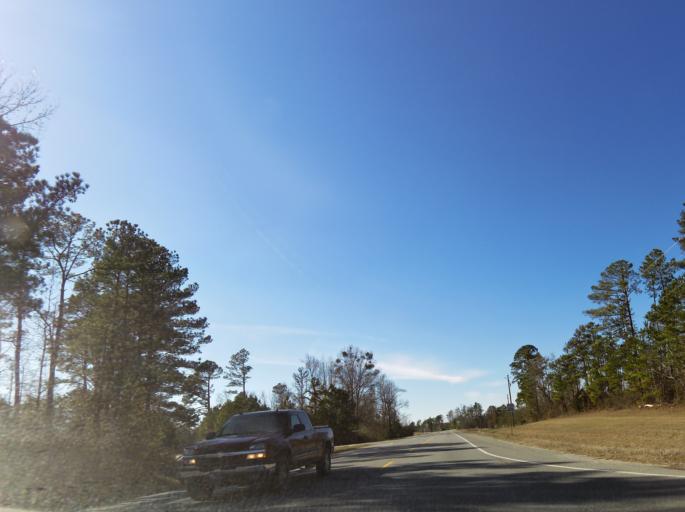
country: US
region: Georgia
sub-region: Bibb County
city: West Point
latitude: 32.8079
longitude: -83.8244
